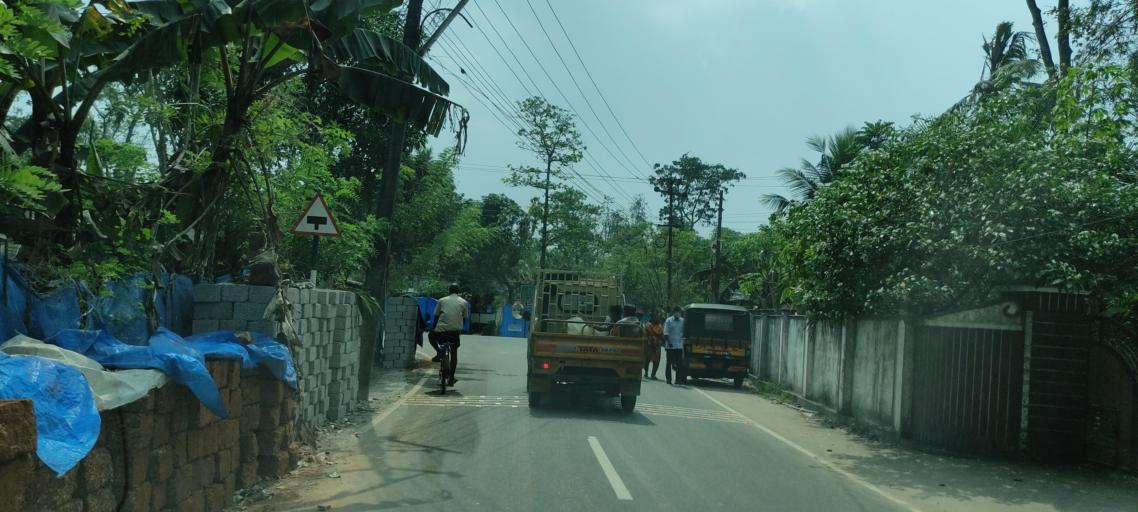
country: IN
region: Kerala
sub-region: Alappuzha
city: Shertallai
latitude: 9.5893
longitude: 76.3385
